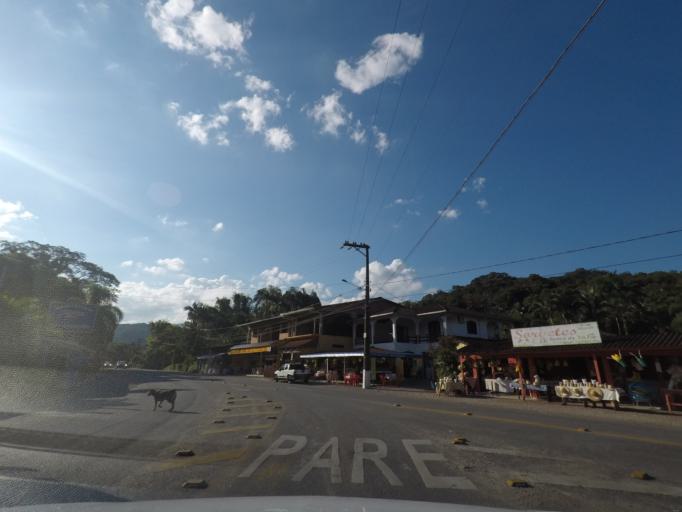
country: BR
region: Parana
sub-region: Antonina
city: Antonina
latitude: -25.3914
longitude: -48.8602
